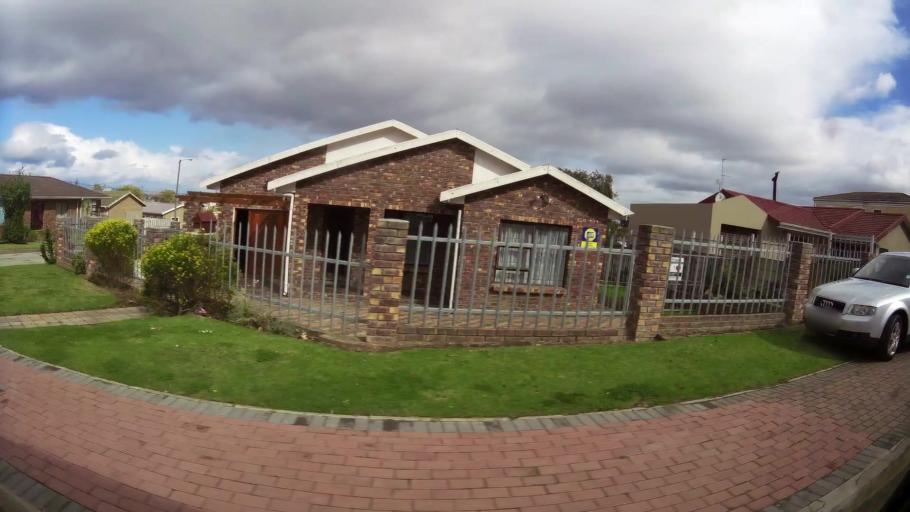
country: ZA
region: Western Cape
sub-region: Eden District Municipality
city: George
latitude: -33.9735
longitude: 22.4881
